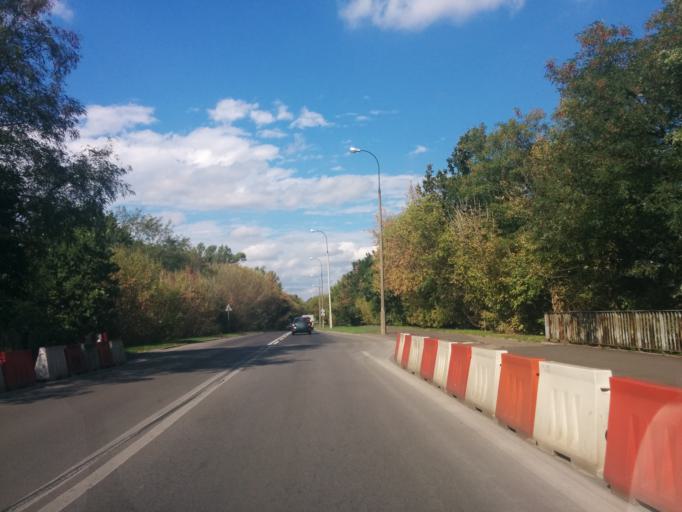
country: PL
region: Masovian Voivodeship
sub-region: Warszawa
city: Bialoleka
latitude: 52.3214
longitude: 20.9958
